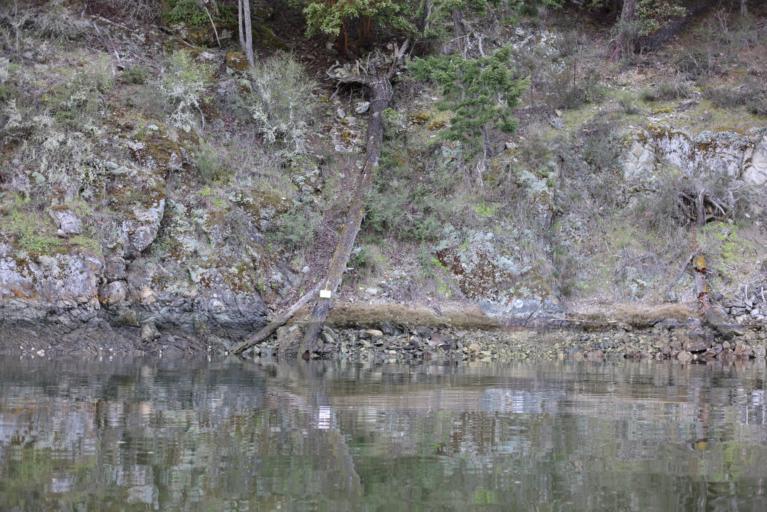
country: CA
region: British Columbia
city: North Saanich
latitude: 48.5686
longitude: -123.4705
